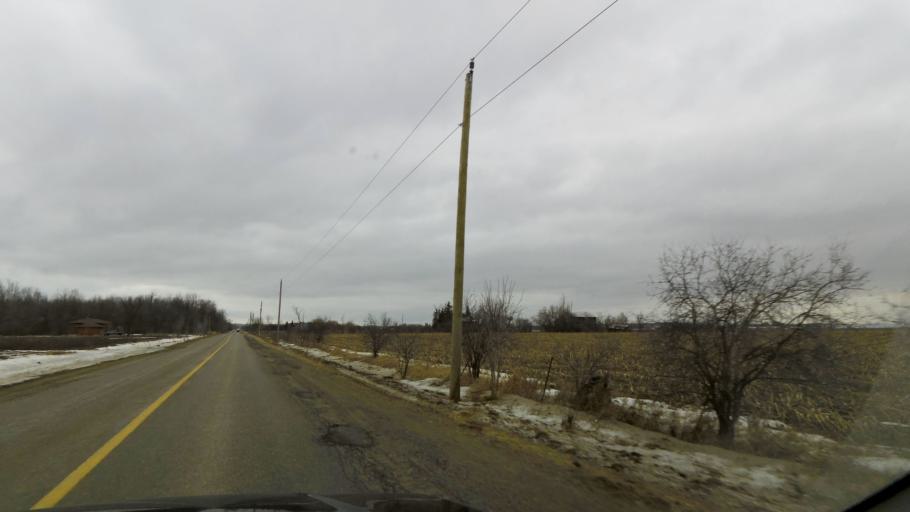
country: CA
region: Ontario
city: Brampton
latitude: 43.8145
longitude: -79.8156
